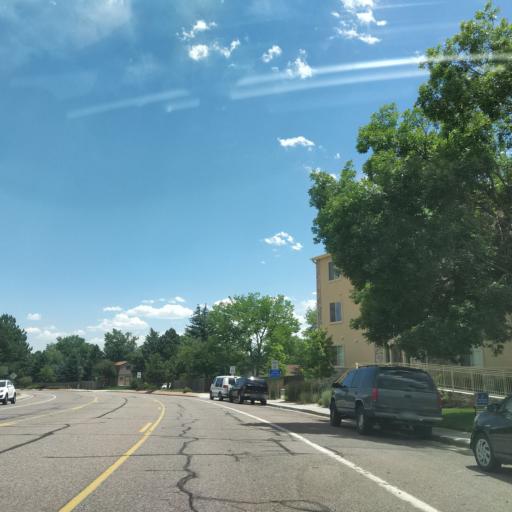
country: US
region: Colorado
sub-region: Jefferson County
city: Lakewood
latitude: 39.6888
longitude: -105.1144
